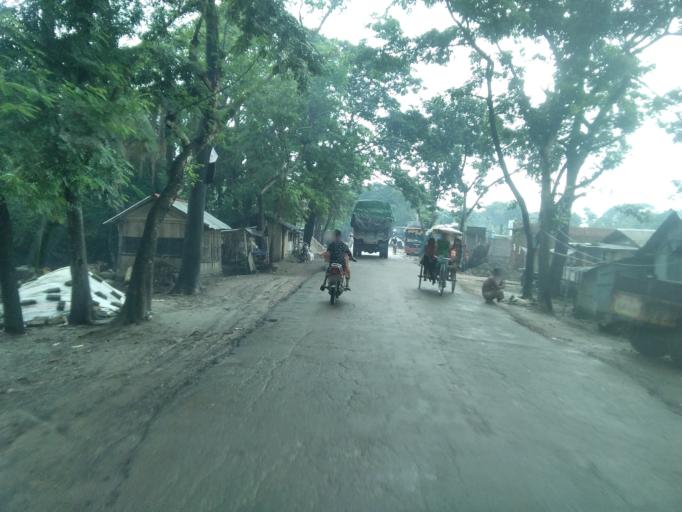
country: IN
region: West Bengal
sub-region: North 24 Parganas
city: Taki
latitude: 22.3488
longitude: 89.1034
